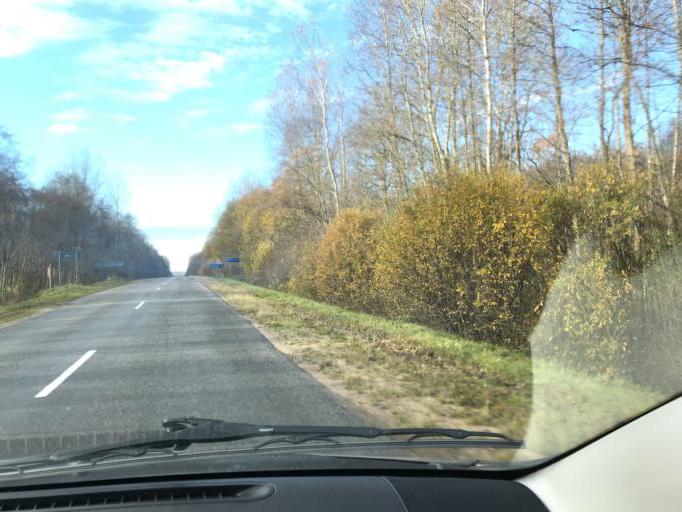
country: BY
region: Vitebsk
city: Haradok
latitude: 55.3940
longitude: 29.6868
